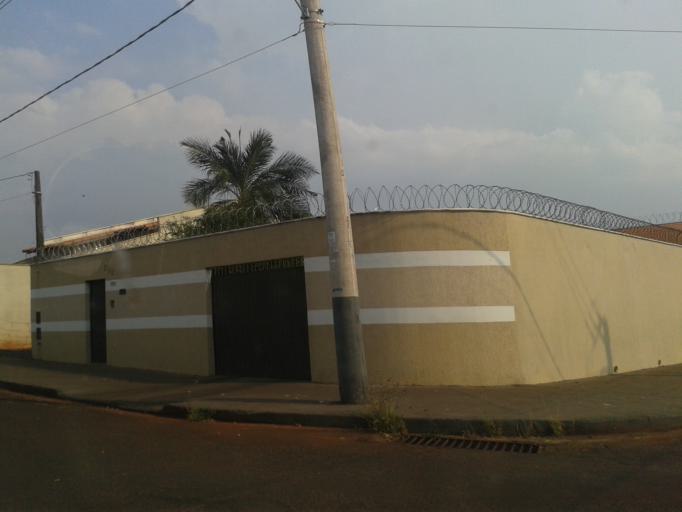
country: BR
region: Minas Gerais
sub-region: Ituiutaba
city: Ituiutaba
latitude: -18.9797
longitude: -49.4847
